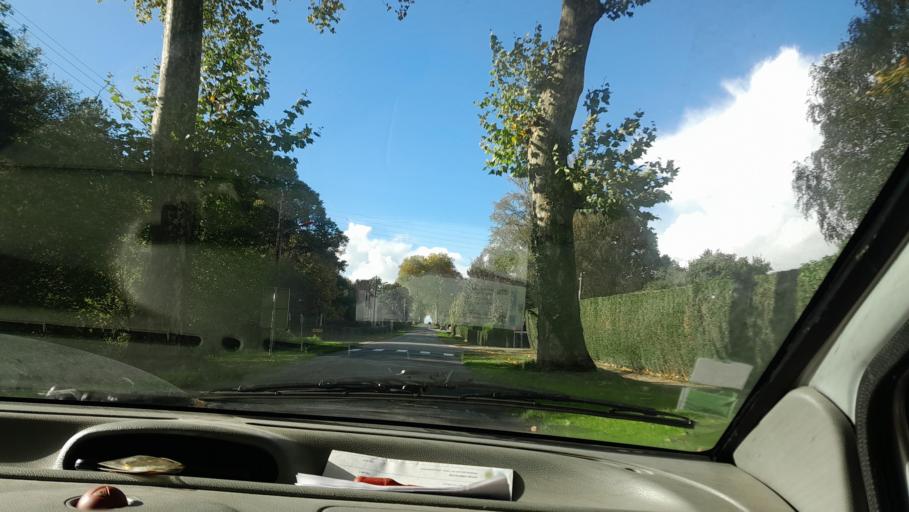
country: FR
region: Pays de la Loire
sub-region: Departement de la Mayenne
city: Cosse-le-Vivien
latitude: 47.9483
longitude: -0.9184
